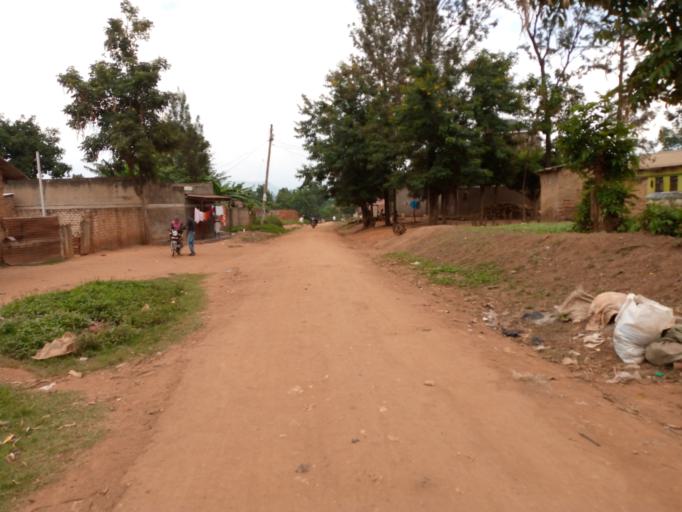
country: UG
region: Eastern Region
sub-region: Mbale District
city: Mbale
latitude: 1.0872
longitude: 34.1655
